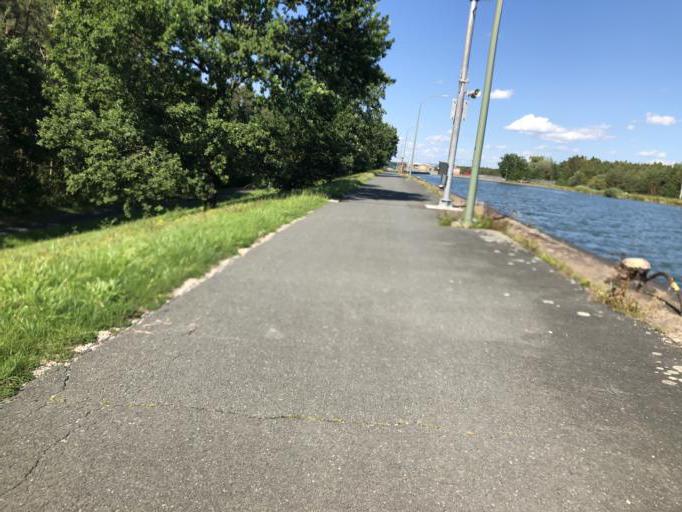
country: DE
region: Bavaria
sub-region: Regierungsbezirk Mittelfranken
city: Mohrendorf
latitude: 49.6197
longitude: 10.9767
